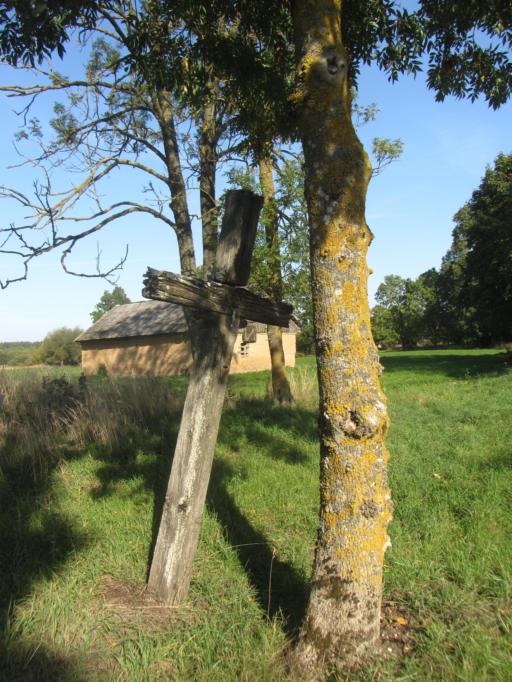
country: LT
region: Siauliu apskritis
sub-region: Joniskis
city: Joniskis
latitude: 56.3422
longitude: 23.6216
